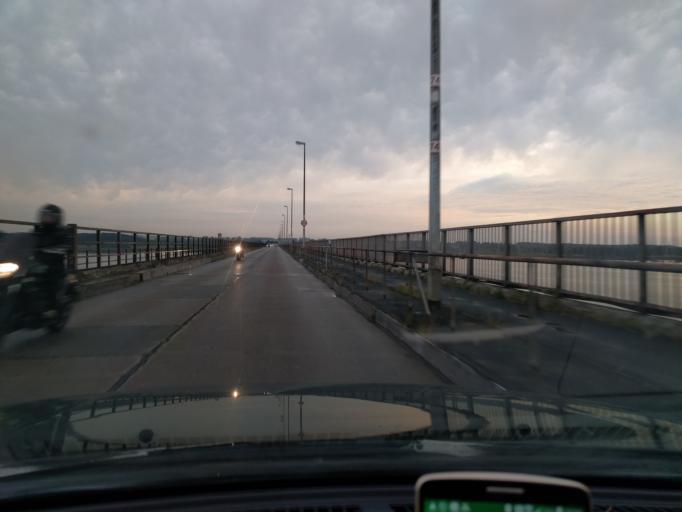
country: DK
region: Zealand
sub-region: Guldborgsund Kommune
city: Norre Alslev
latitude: 54.9577
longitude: 11.8751
